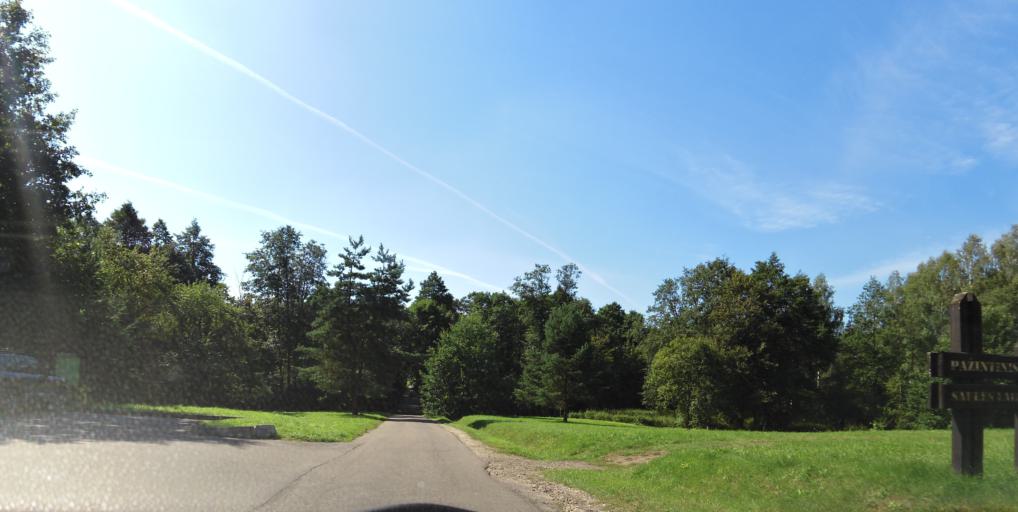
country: LT
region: Vilnius County
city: Rasos
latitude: 54.6891
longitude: 25.3682
